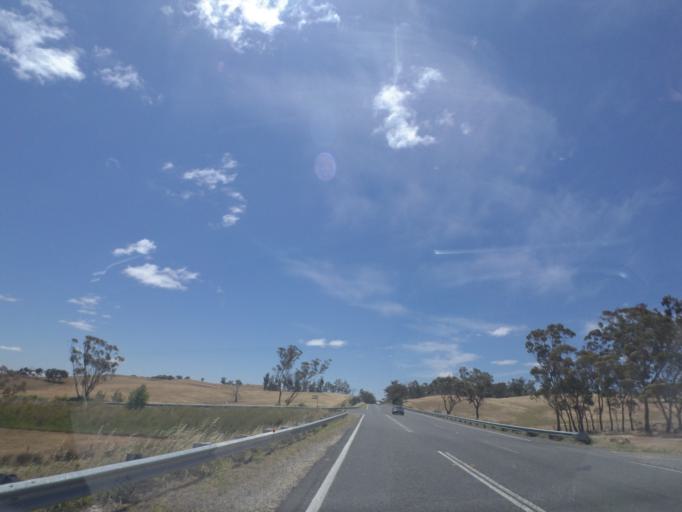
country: AU
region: Victoria
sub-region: Mount Alexander
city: Castlemaine
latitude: -37.2101
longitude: 144.1404
